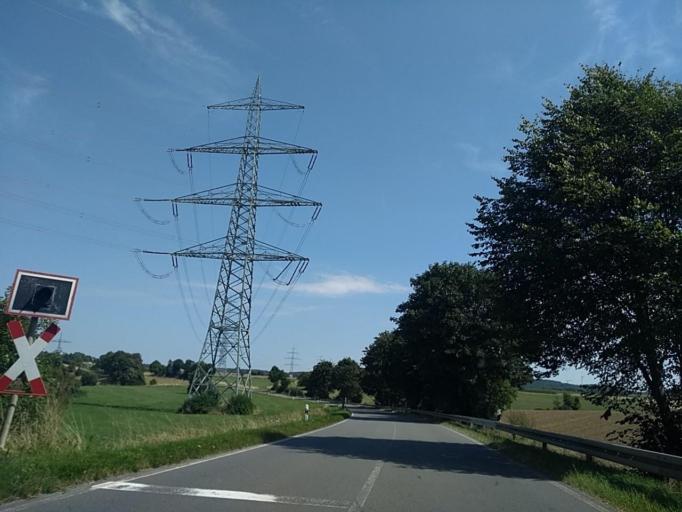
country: DE
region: North Rhine-Westphalia
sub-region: Regierungsbezirk Arnsberg
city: Brilon
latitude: 51.4264
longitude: 8.6248
